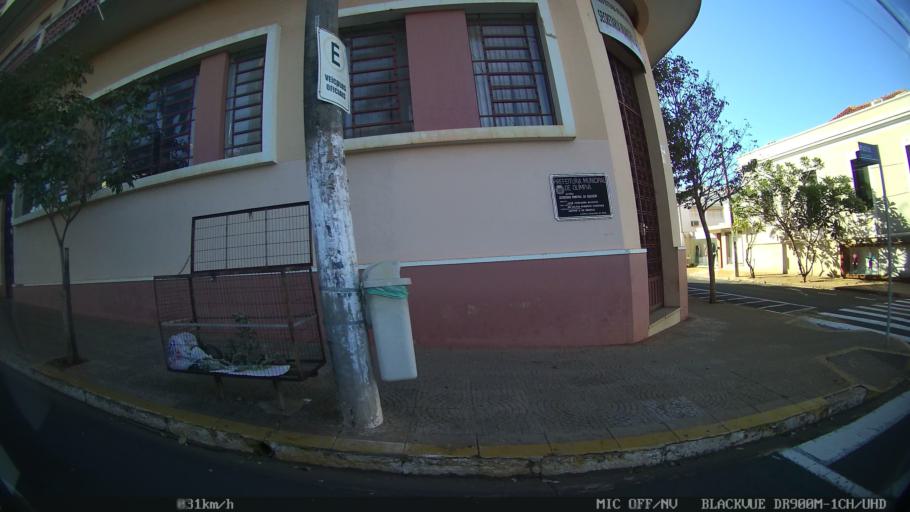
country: BR
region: Sao Paulo
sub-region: Olimpia
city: Olimpia
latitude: -20.7377
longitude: -48.9145
